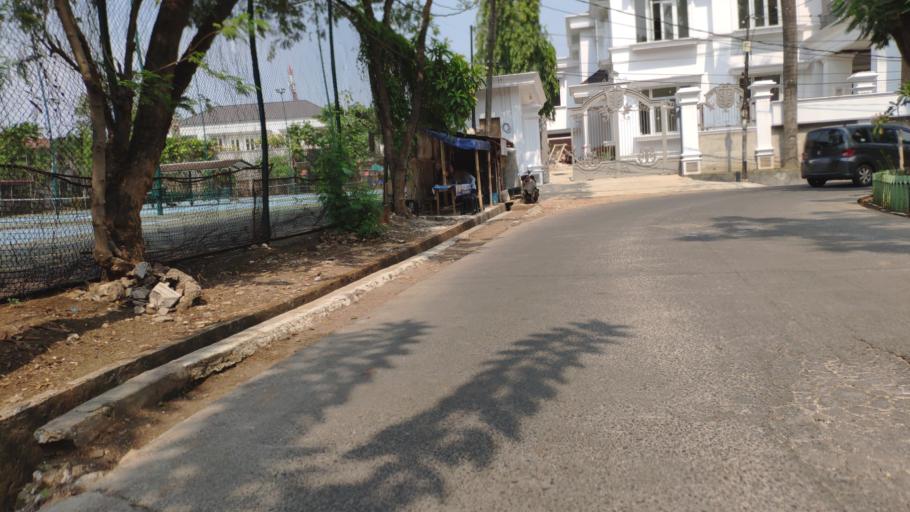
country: ID
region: Jakarta Raya
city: Jakarta
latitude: -6.2606
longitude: 106.8257
